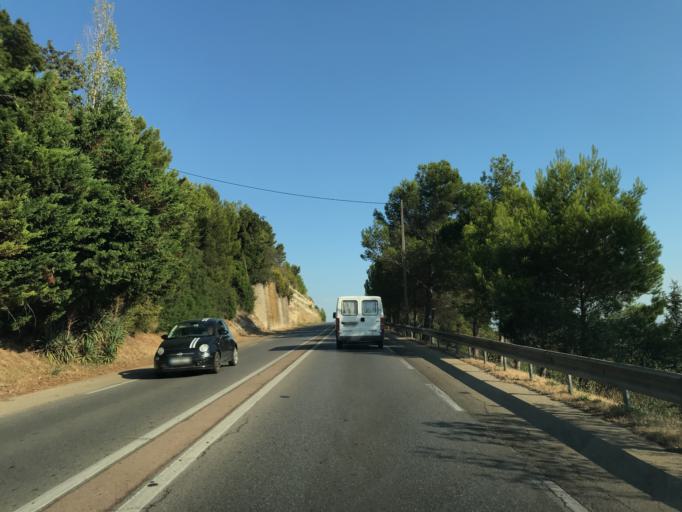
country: FR
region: Provence-Alpes-Cote d'Azur
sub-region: Departement des Bouches-du-Rhone
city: Saint-Chamas
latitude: 43.5535
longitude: 5.0349
